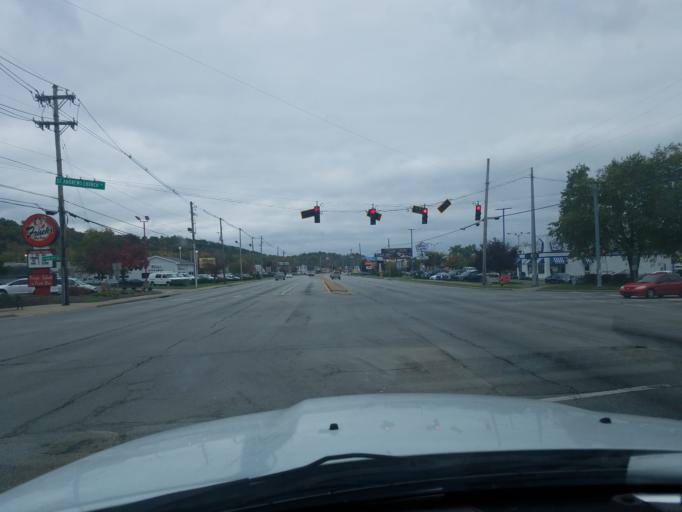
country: US
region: Kentucky
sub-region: Jefferson County
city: Pleasure Ridge Park
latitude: 38.1437
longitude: -85.8395
